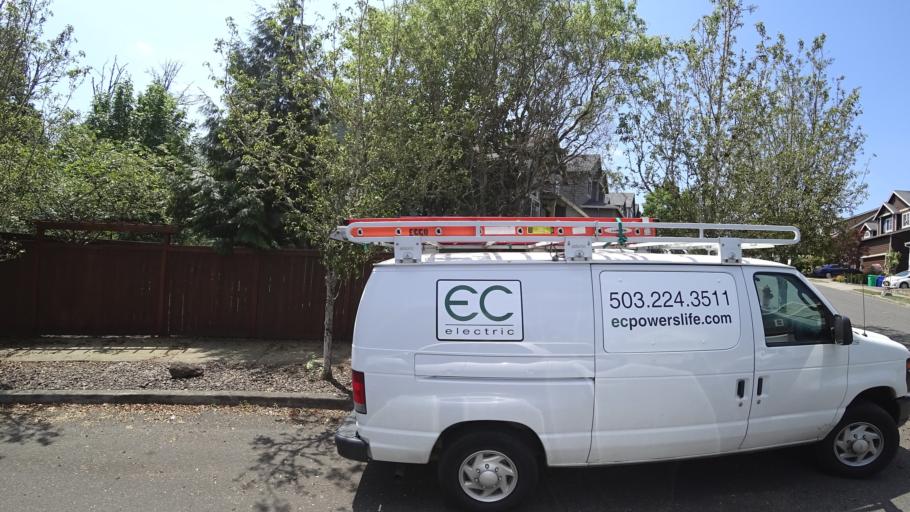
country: US
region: Oregon
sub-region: Clackamas County
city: Happy Valley
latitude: 45.4679
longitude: -122.4998
